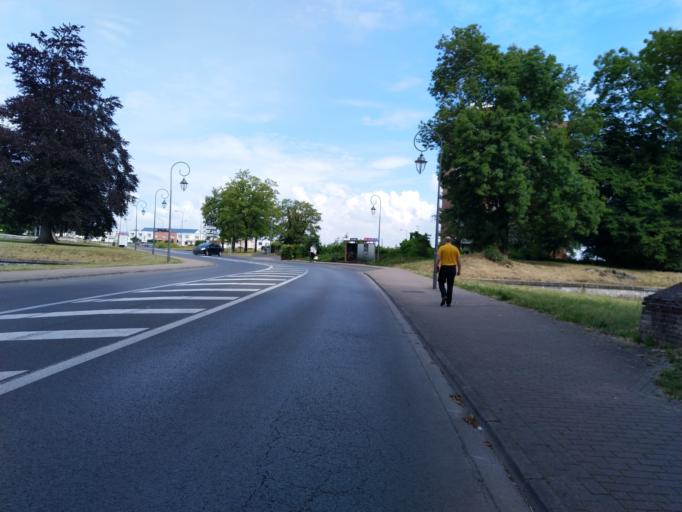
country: FR
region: Nord-Pas-de-Calais
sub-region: Departement du Nord
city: Maubeuge
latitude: 50.2812
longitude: 3.9760
